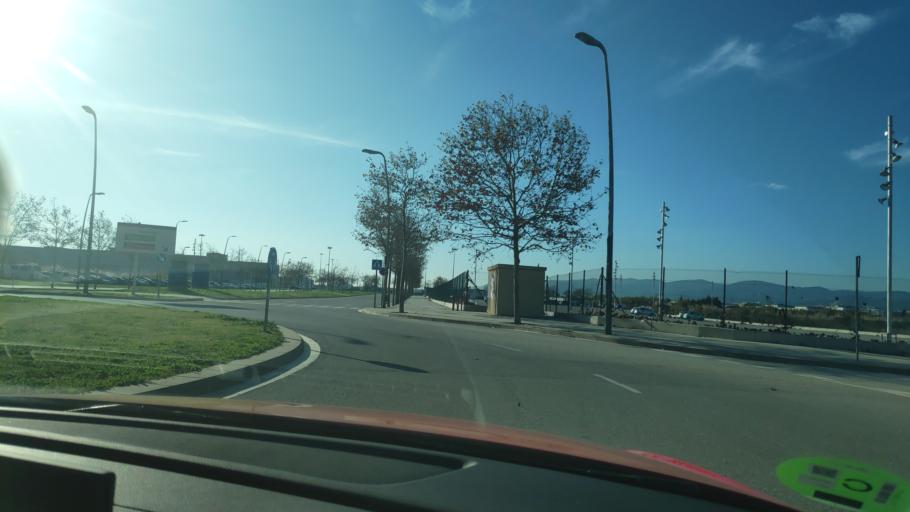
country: ES
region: Catalonia
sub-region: Provincia de Barcelona
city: El Prat de Llobregat
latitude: 41.3102
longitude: 2.0858
